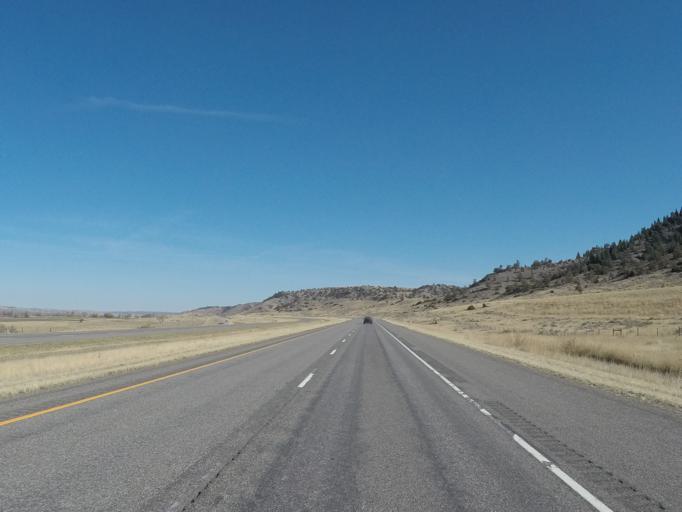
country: US
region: Montana
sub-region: Sweet Grass County
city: Big Timber
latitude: 45.7641
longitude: -110.0972
